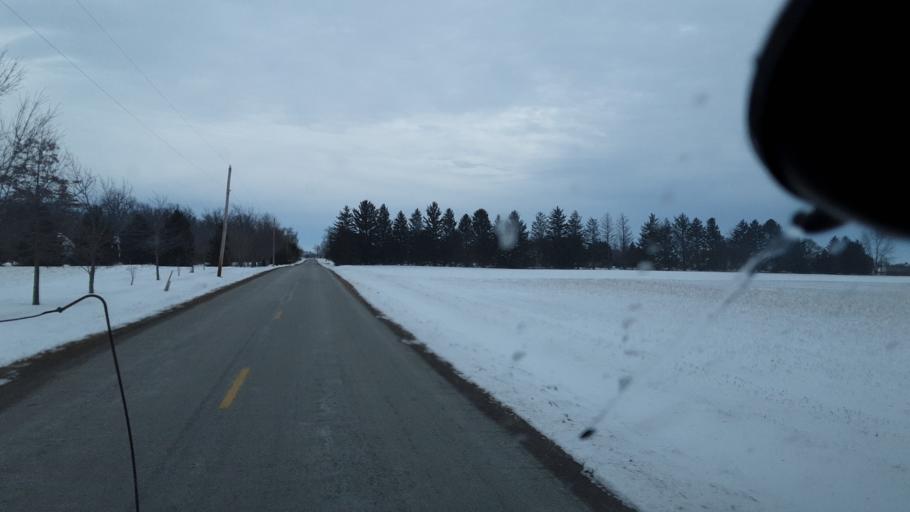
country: US
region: Ohio
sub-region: Madison County
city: Bethel
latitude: 39.7180
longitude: -83.3824
